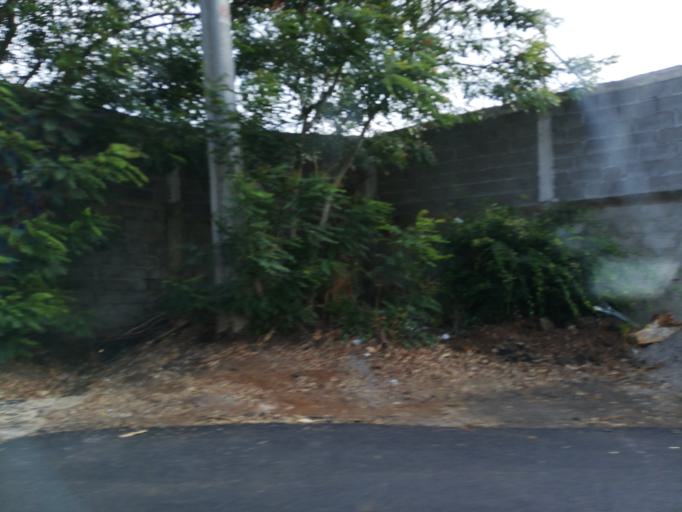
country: MU
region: Black River
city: Petite Riviere
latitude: -20.2254
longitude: 57.4579
